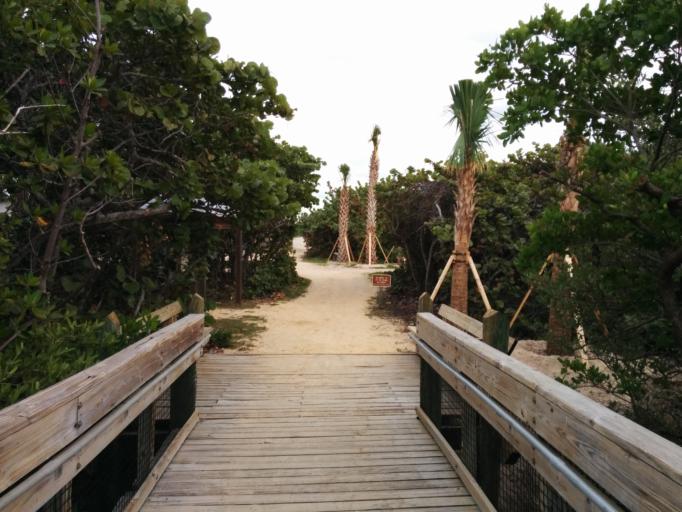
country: US
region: Florida
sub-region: Broward County
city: Dania Beach
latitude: 26.0666
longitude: -80.1120
